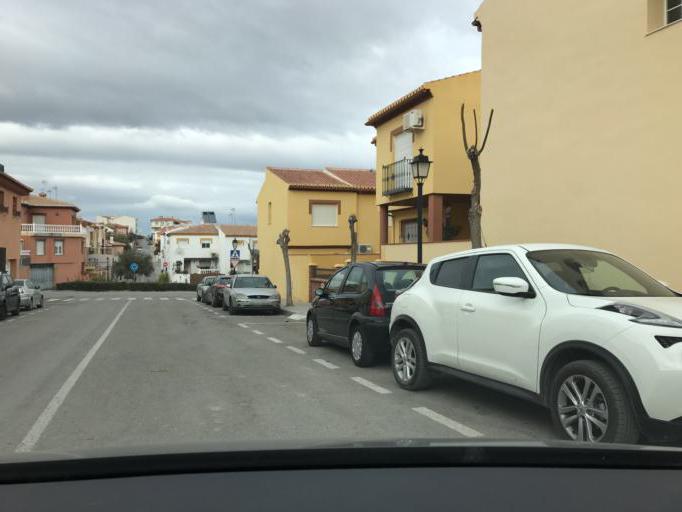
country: ES
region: Andalusia
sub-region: Provincia de Granada
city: Las Gabias
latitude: 37.1303
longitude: -3.6780
